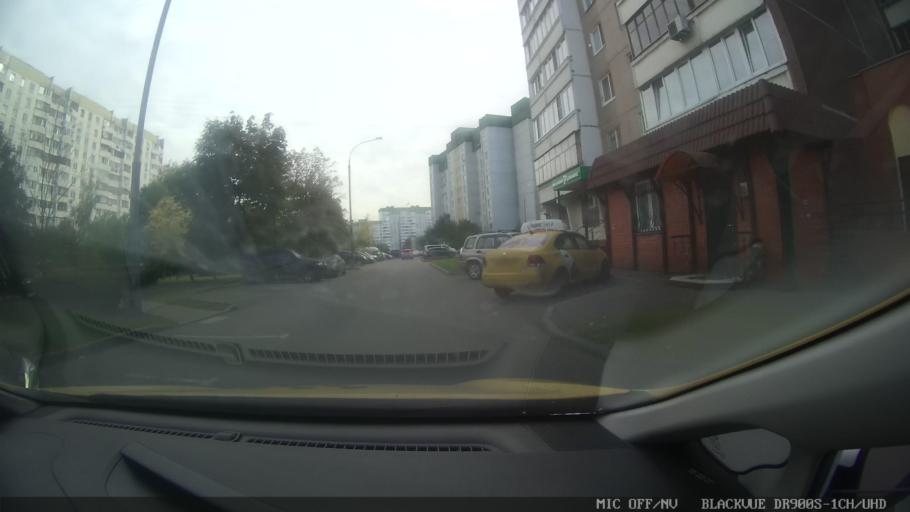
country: RU
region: Moscow
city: Zhulebino
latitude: 55.6856
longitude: 37.8479
